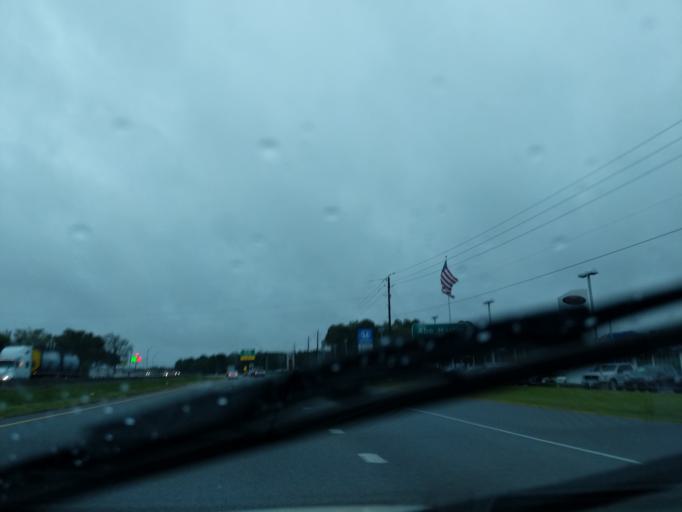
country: US
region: Texas
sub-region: Angelina County
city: Lufkin
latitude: 31.3236
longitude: -94.6949
